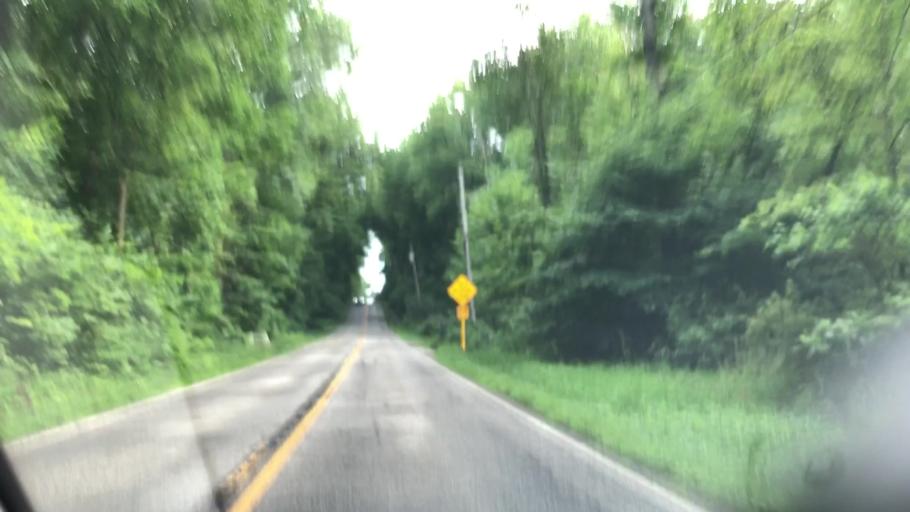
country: US
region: Ohio
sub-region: Summit County
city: Montrose-Ghent
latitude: 41.1259
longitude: -81.7158
